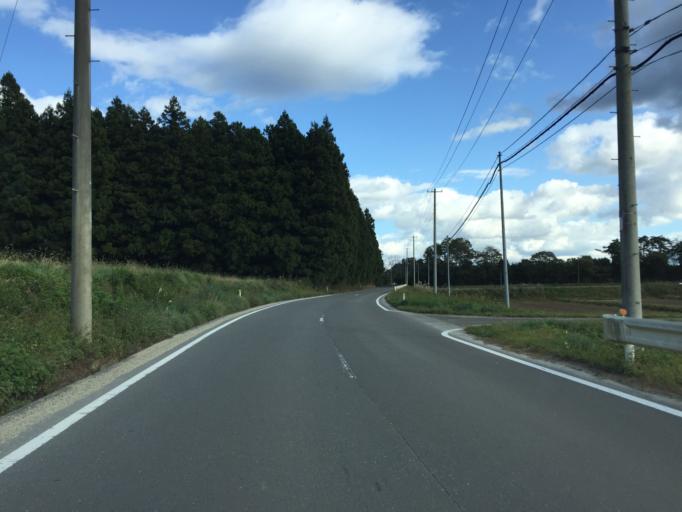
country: JP
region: Miyagi
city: Marumori
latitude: 37.8350
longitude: 140.8192
